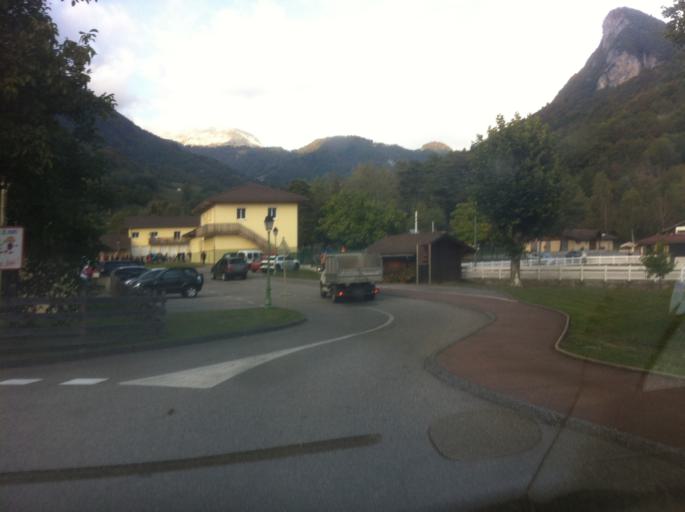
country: FR
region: Rhone-Alpes
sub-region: Departement de la Haute-Savoie
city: Faverges
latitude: 45.7653
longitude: 6.3090
